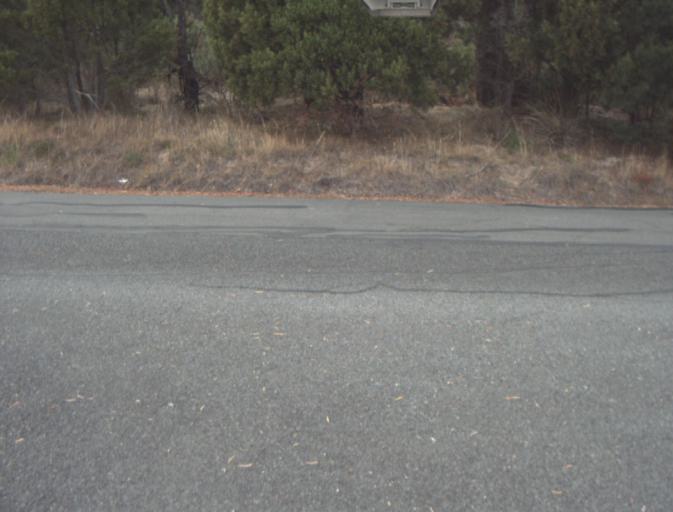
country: AU
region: Tasmania
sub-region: Launceston
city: Mayfield
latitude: -41.3291
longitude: 147.0585
